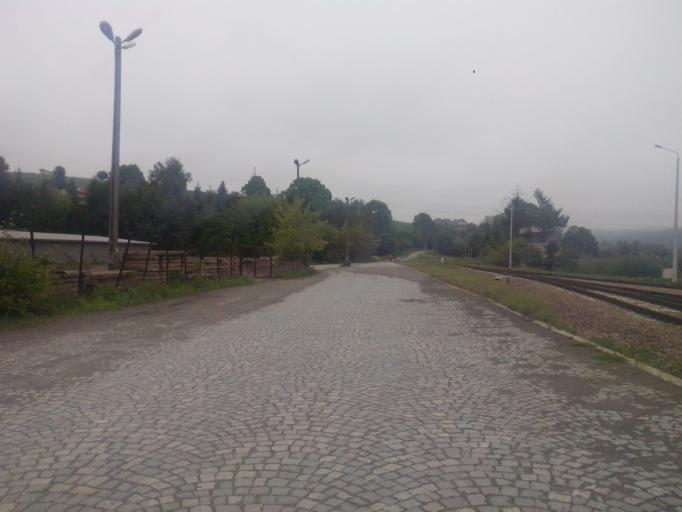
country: PL
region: Subcarpathian Voivodeship
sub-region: Powiat strzyzowski
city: Strzyzow
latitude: 49.8693
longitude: 21.8051
